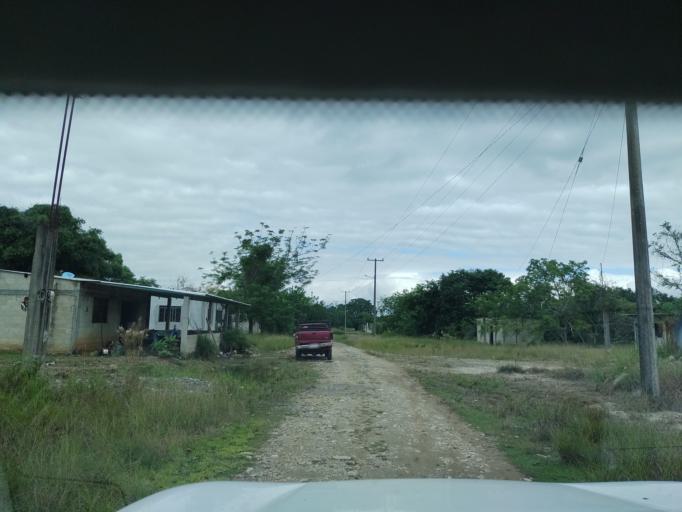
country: MX
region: Veracruz
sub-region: Atzalan
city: Colonias Pedernales
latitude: 20.0384
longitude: -97.0723
